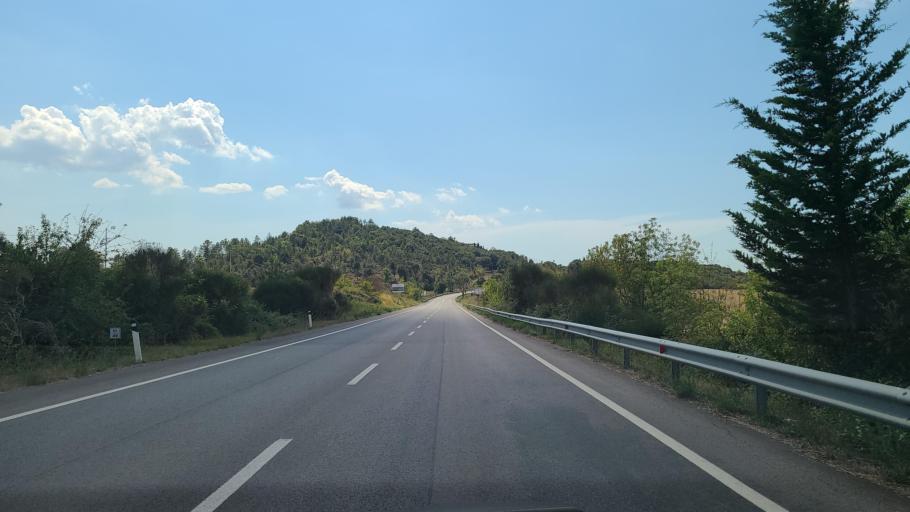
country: IT
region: Tuscany
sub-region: Provincia di Siena
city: San Gimignano
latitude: 43.3985
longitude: 10.9629
